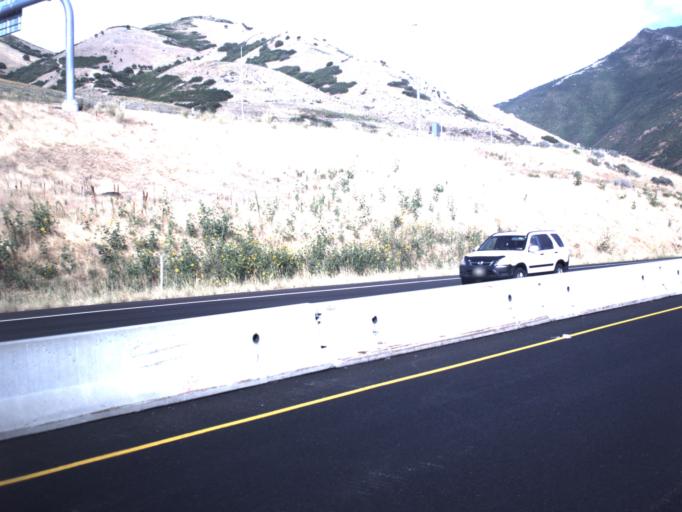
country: US
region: Utah
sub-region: Salt Lake County
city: East Millcreek
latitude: 40.7130
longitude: -111.8087
